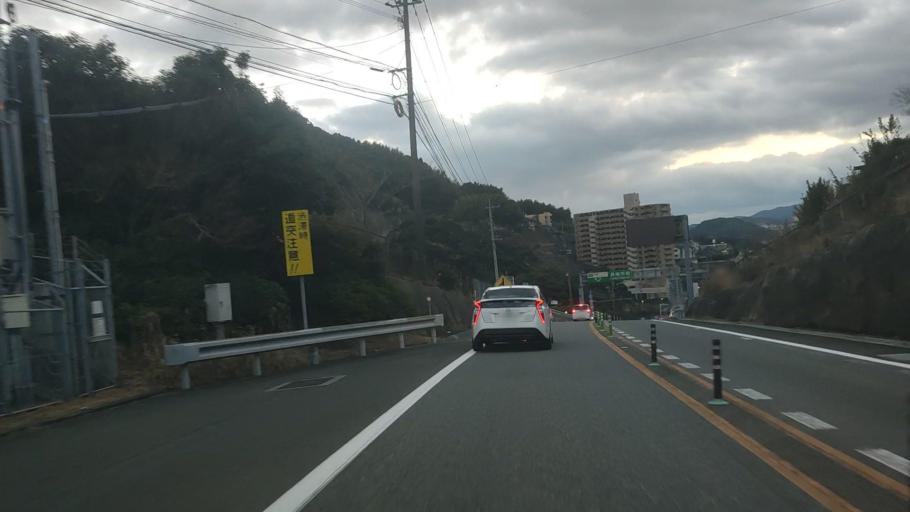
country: JP
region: Nagasaki
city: Nagasaki-shi
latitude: 32.7707
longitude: 129.8911
